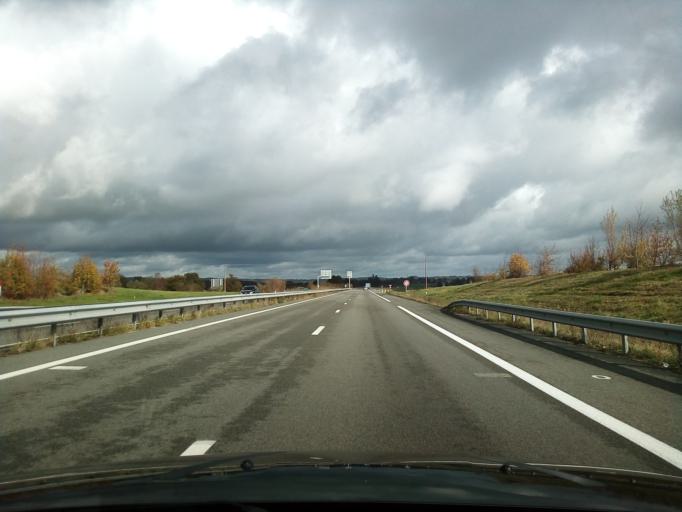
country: FR
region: Limousin
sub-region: Departement de la Creuse
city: Chambon-sur-Voueize
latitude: 46.2594
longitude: 2.3627
